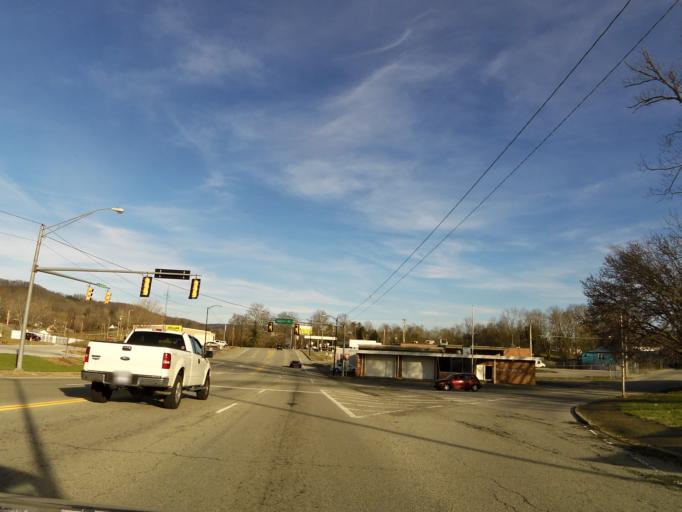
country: US
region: Tennessee
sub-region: White County
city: Sparta
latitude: 35.9246
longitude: -85.4590
